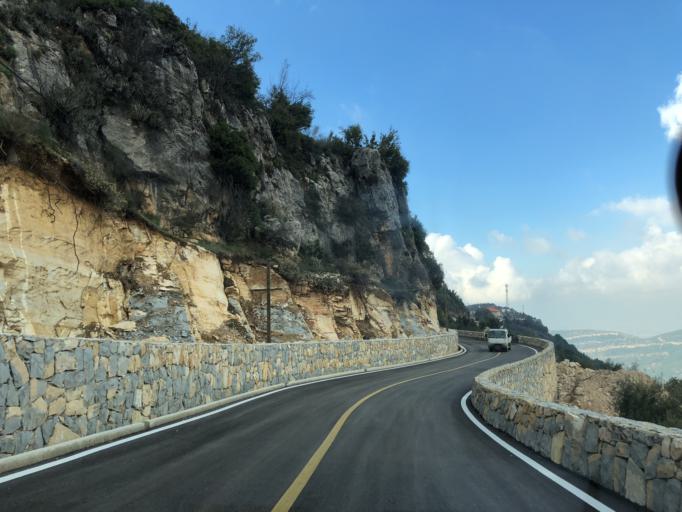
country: LB
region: Liban-Nord
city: Amioun
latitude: 34.2125
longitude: 35.8306
